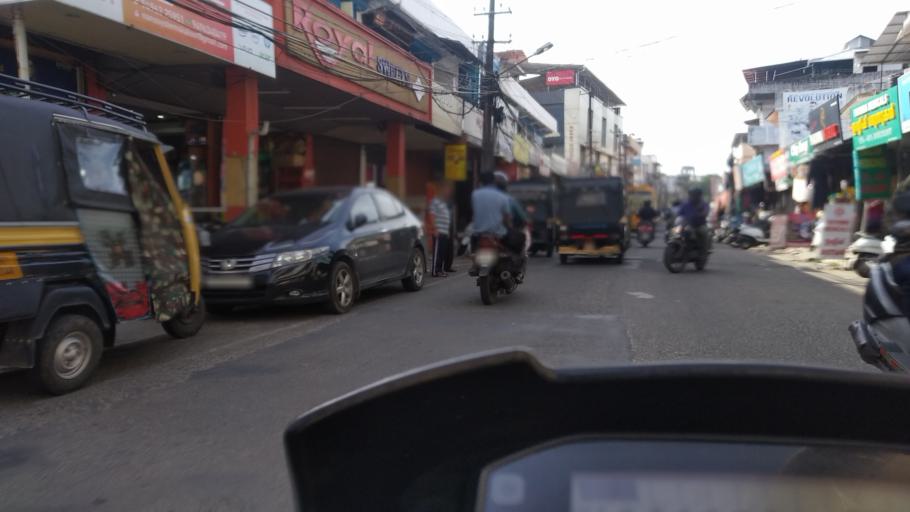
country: IN
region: Kerala
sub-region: Ernakulam
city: Elur
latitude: 10.0048
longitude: 76.2952
